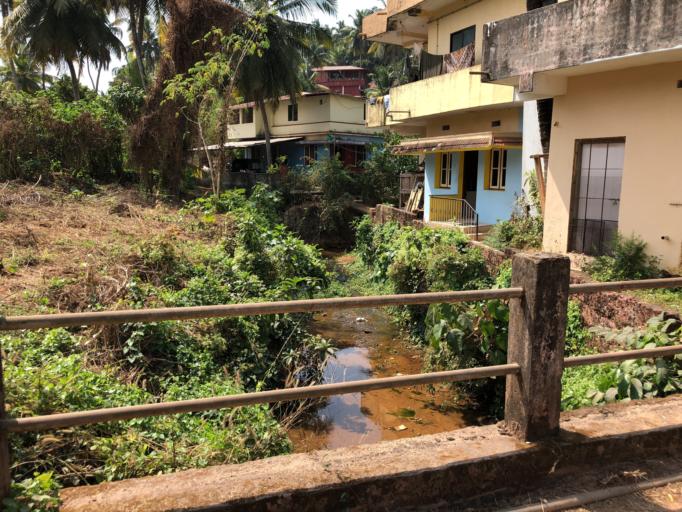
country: IN
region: Karnataka
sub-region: Dakshina Kannada
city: Mangalore
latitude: 12.8773
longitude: 74.8710
